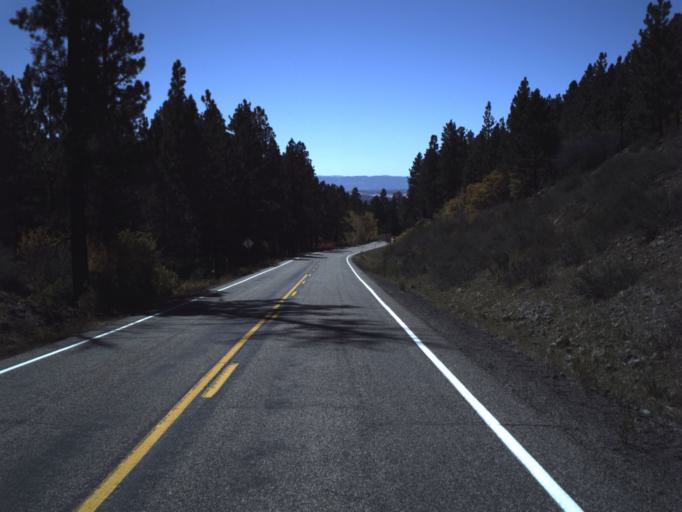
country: US
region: Utah
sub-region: Wayne County
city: Loa
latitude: 37.9967
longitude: -111.4173
